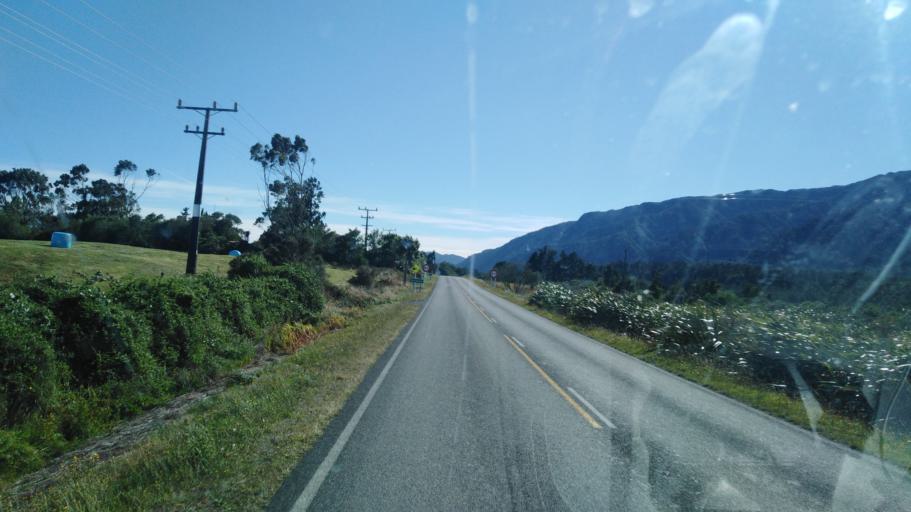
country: NZ
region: West Coast
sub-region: Buller District
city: Westport
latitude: -41.6802
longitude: 171.7923
